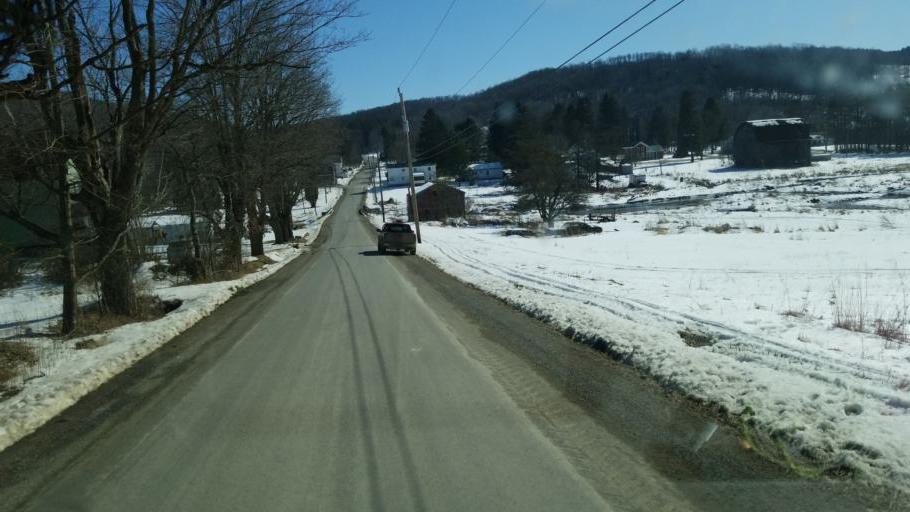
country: US
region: New York
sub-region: Allegany County
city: Andover
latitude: 42.0857
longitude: -77.6644
